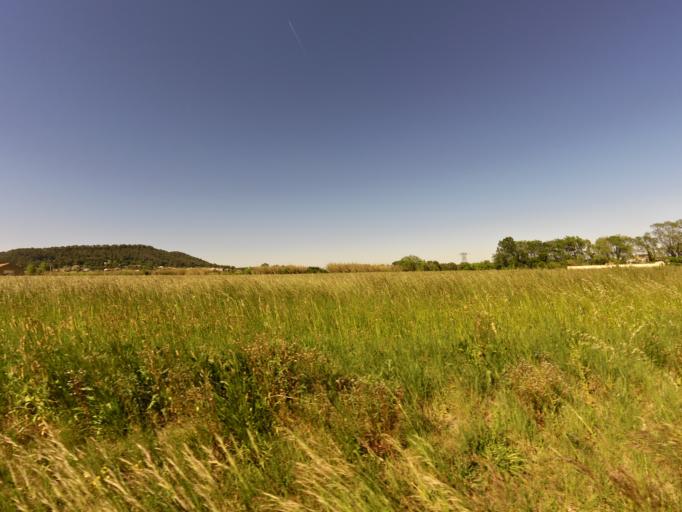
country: FR
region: Languedoc-Roussillon
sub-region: Departement du Gard
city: Sommieres
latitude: 43.8311
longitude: 4.0307
